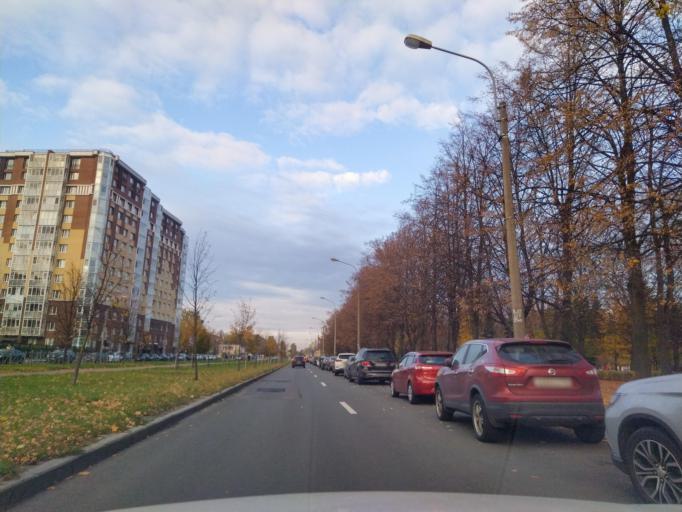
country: RU
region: Leningrad
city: Kalininskiy
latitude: 59.9698
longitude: 30.3962
